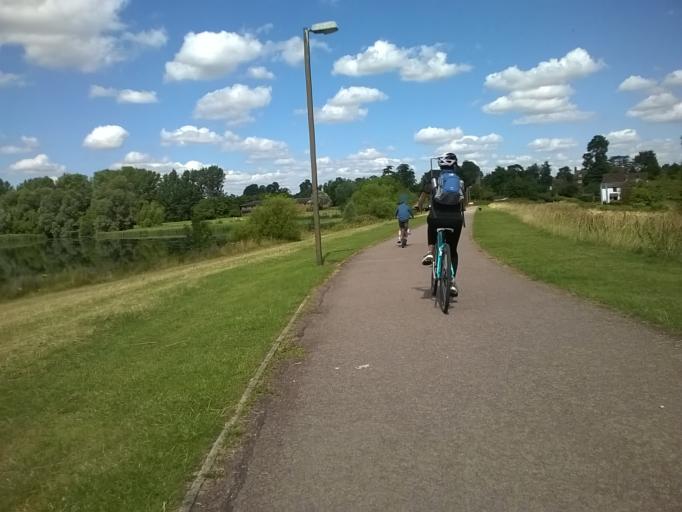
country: GB
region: England
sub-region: Milton Keynes
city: Broughton
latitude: 52.0599
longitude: -0.7177
